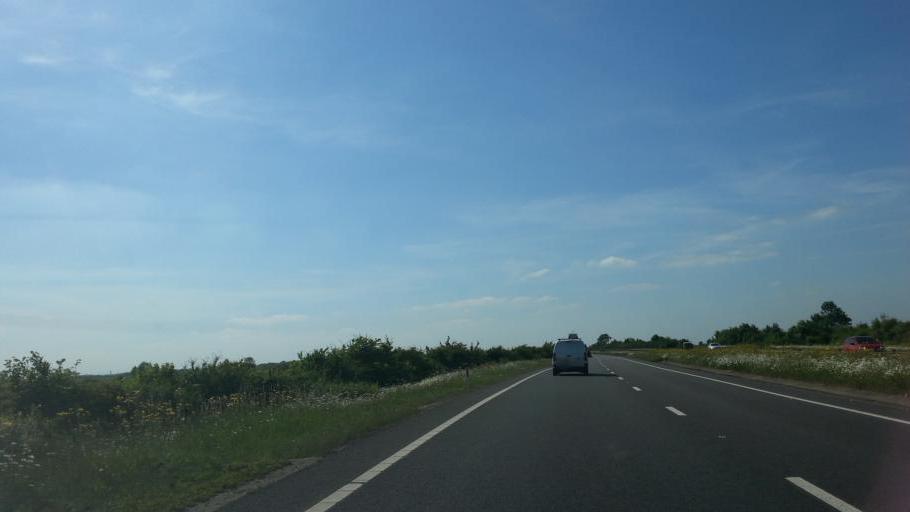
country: GB
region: England
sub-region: Cambridgeshire
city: Papworth Everard
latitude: 52.2261
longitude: -0.0789
